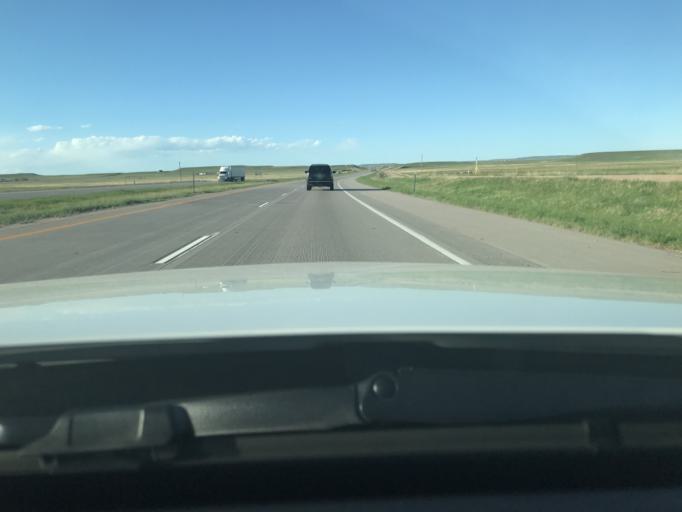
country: US
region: Colorado
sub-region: Larimer County
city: Wellington
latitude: 40.8965
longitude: -104.9477
